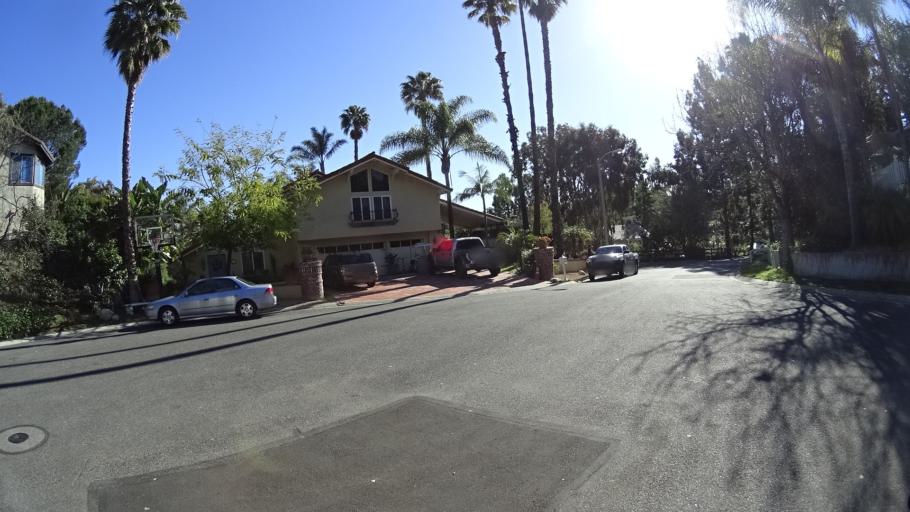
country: US
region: California
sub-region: Ventura County
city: Casa Conejo
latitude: 34.1865
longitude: -118.9050
